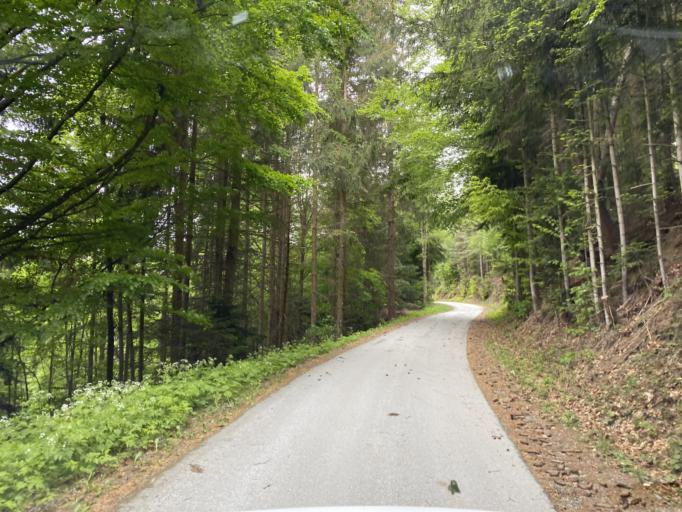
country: AT
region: Styria
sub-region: Politischer Bezirk Weiz
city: Koglhof
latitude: 47.3242
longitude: 15.7022
